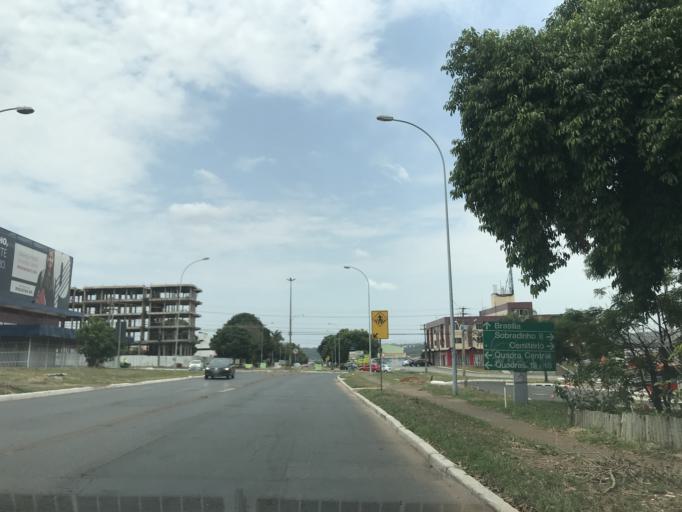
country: BR
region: Federal District
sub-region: Brasilia
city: Brasilia
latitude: -15.6555
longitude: -47.8049
